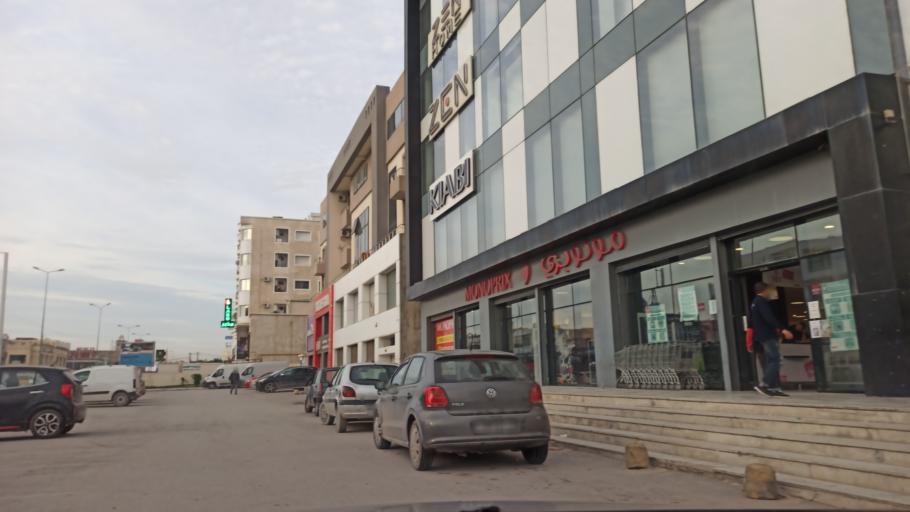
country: TN
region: Ariana
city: Ariana
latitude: 36.8642
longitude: 10.2158
